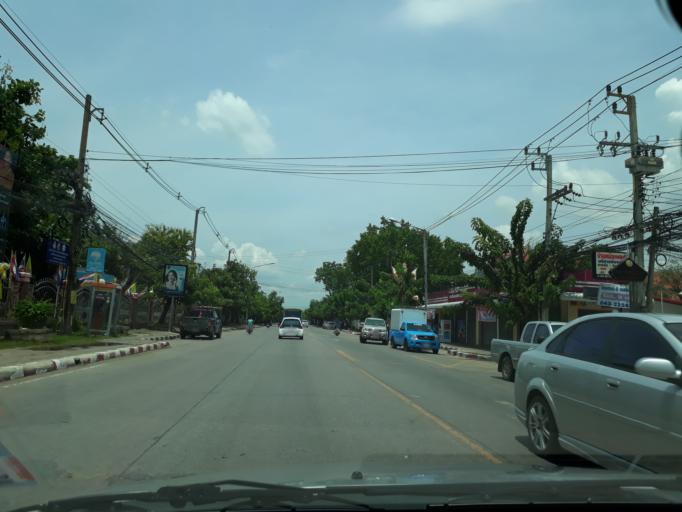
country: TH
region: Khon Kaen
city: Khon Kaen
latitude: 16.4151
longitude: 102.8245
